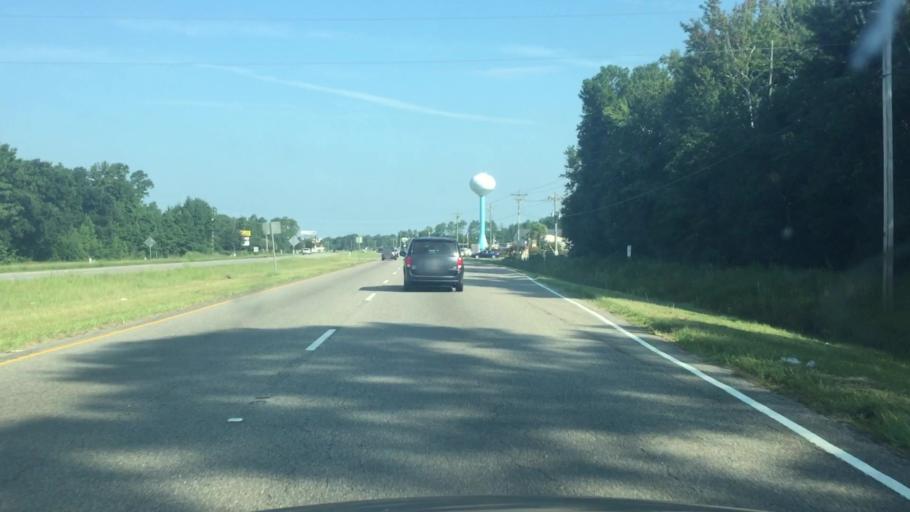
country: US
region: South Carolina
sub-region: Horry County
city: North Myrtle Beach
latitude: 33.8979
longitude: -78.6969
